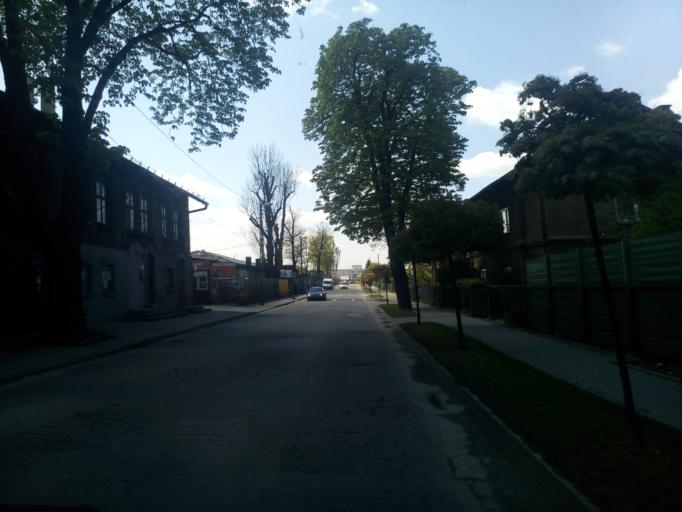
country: PL
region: Lesser Poland Voivodeship
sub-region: Powiat nowosadecki
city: Nowy Sacz
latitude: 49.6062
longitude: 20.6996
